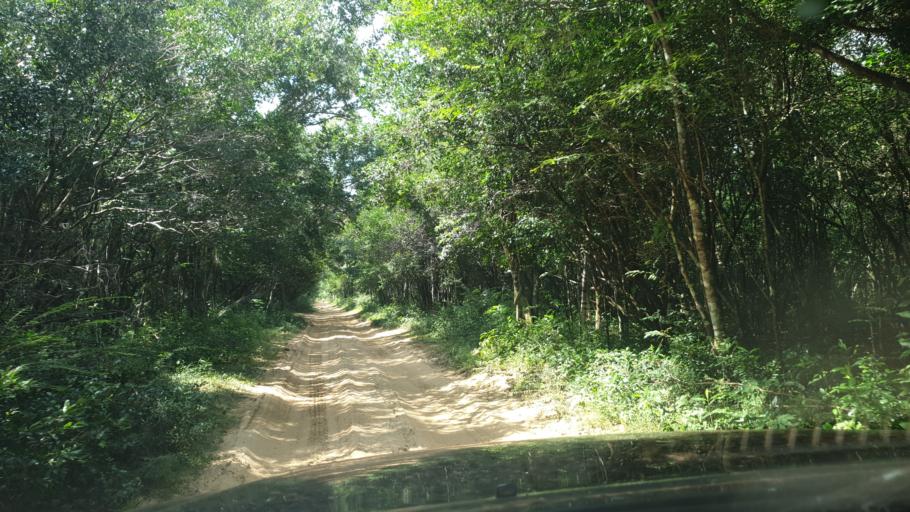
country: LK
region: North Central
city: Anuradhapura
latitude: 8.4180
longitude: 80.0212
